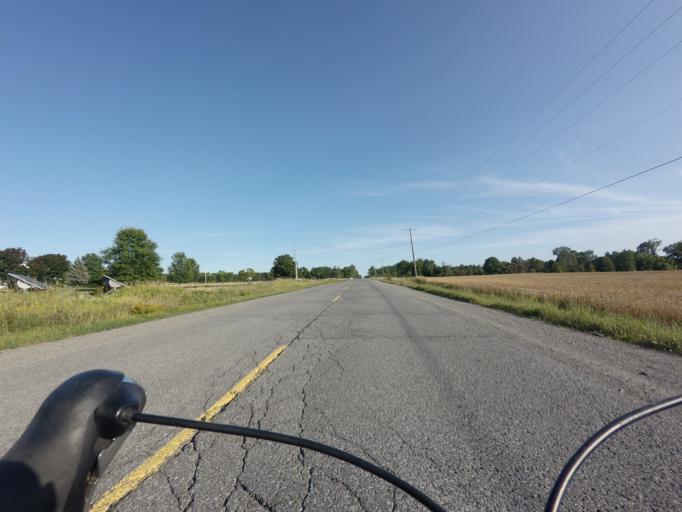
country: CA
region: Ontario
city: Bells Corners
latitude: 45.4636
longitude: -76.0031
